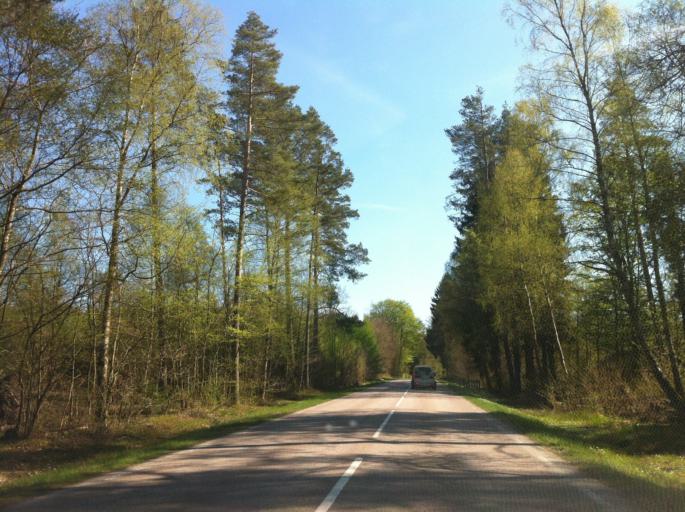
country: SE
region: Skane
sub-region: Svalovs Kommun
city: Kagerod
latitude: 56.0492
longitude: 13.1029
